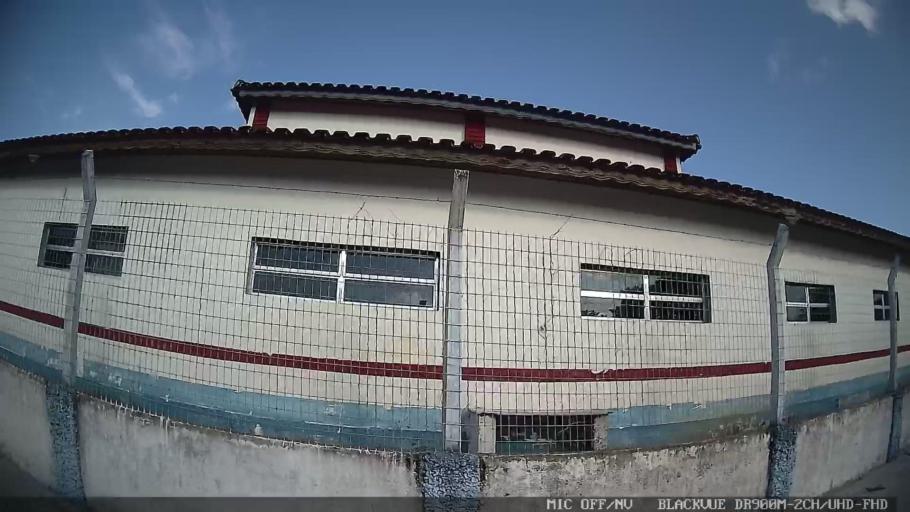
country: BR
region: Sao Paulo
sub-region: Itanhaem
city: Itanhaem
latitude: -24.1735
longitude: -46.8185
